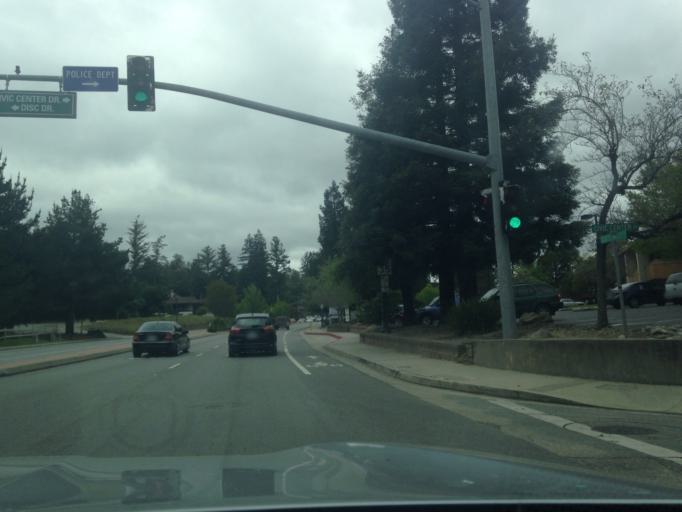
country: US
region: California
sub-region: Santa Cruz County
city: Scotts Valley
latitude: 37.0485
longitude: -122.0169
